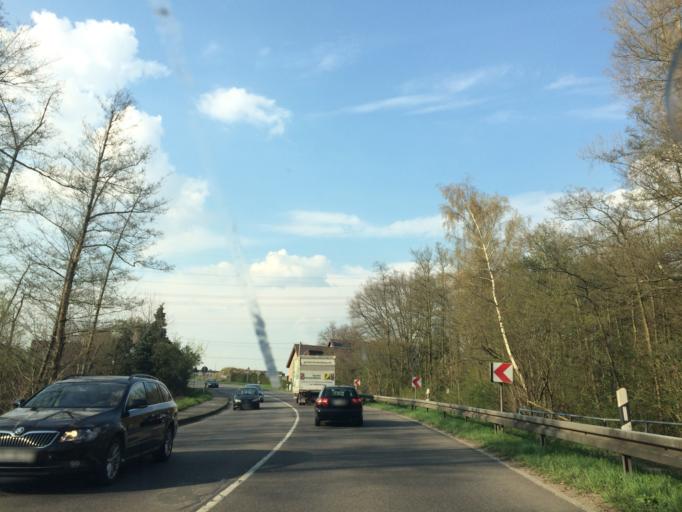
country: DE
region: North Rhine-Westphalia
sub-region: Regierungsbezirk Munster
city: Bottrop
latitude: 51.5630
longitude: 6.9128
